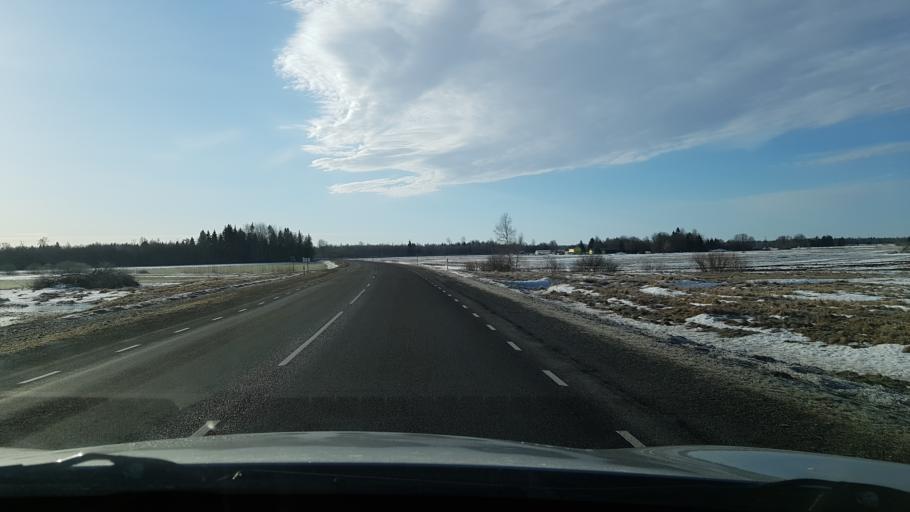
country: EE
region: Viljandimaa
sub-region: Vohma linn
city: Vohma
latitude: 58.6248
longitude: 25.5692
